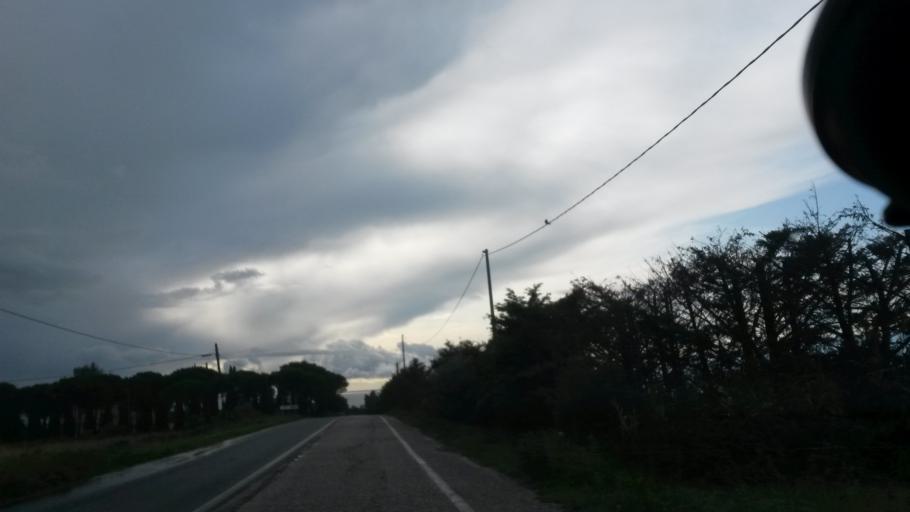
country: IT
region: Tuscany
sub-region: Provincia di Livorno
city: Rosignano Marittimo
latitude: 43.4176
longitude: 10.4543
